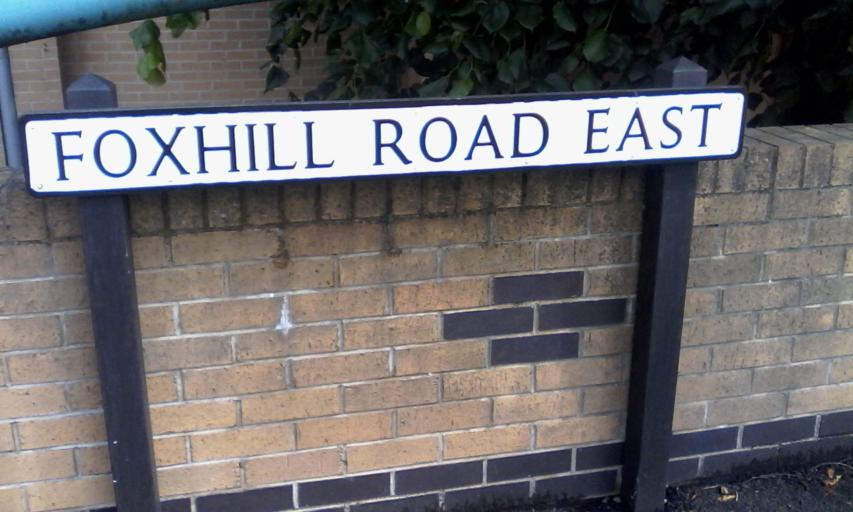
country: GB
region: England
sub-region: Nottinghamshire
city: West Bridgford
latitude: 52.9679
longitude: -1.0898
